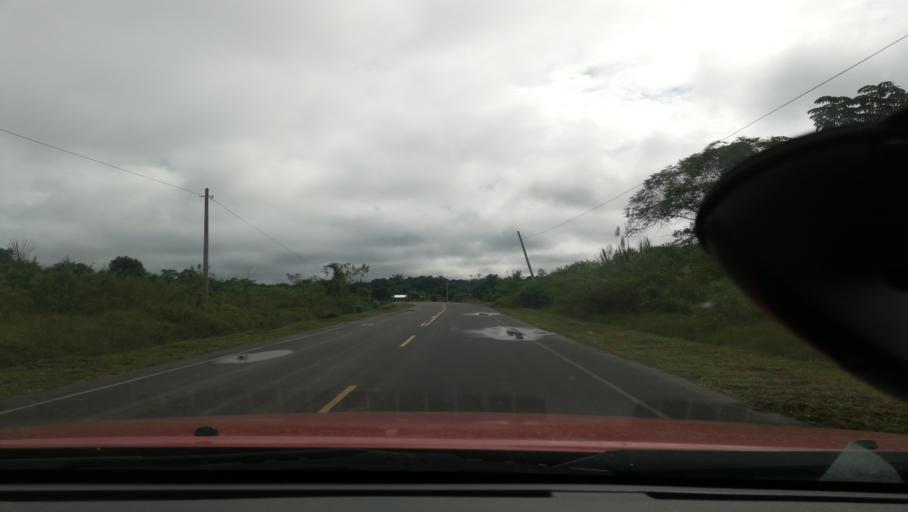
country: PE
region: Loreto
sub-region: Provincia de Loreto
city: Nauta
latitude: -4.3324
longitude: -73.5337
